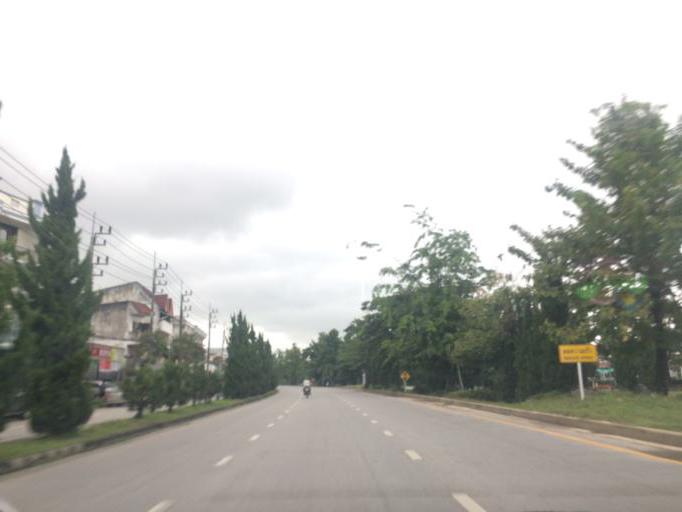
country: TH
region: Chiang Rai
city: Chiang Rai
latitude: 19.9047
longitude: 99.8408
